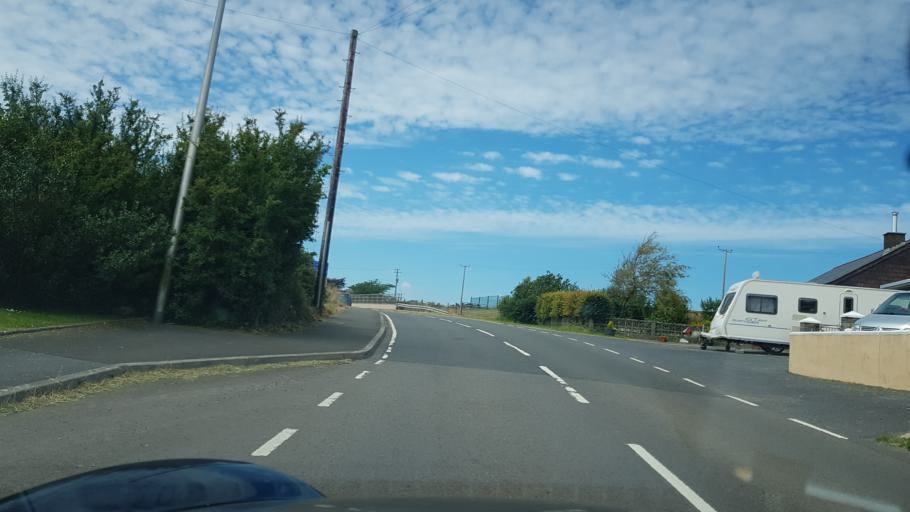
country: GB
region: Wales
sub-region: Carmarthenshire
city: Whitland
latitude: 51.7768
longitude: -4.6070
